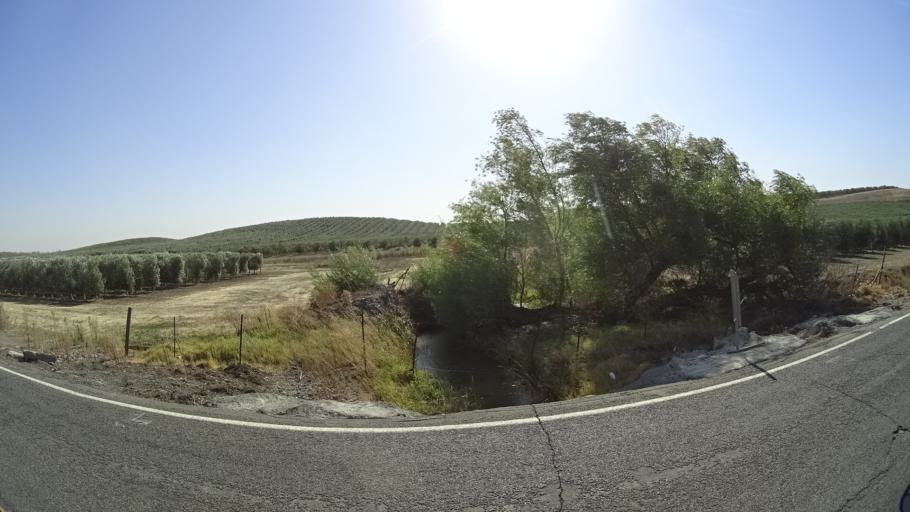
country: US
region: California
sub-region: Yolo County
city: Cottonwood
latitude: 38.7087
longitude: -121.8840
